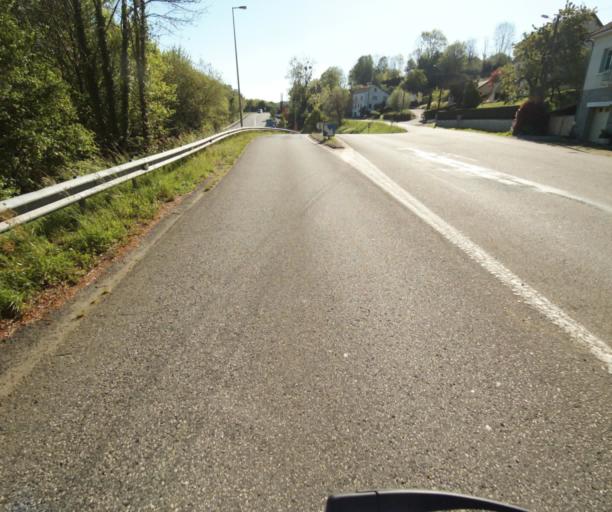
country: FR
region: Limousin
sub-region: Departement de la Correze
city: Tulle
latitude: 45.2728
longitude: 1.7848
